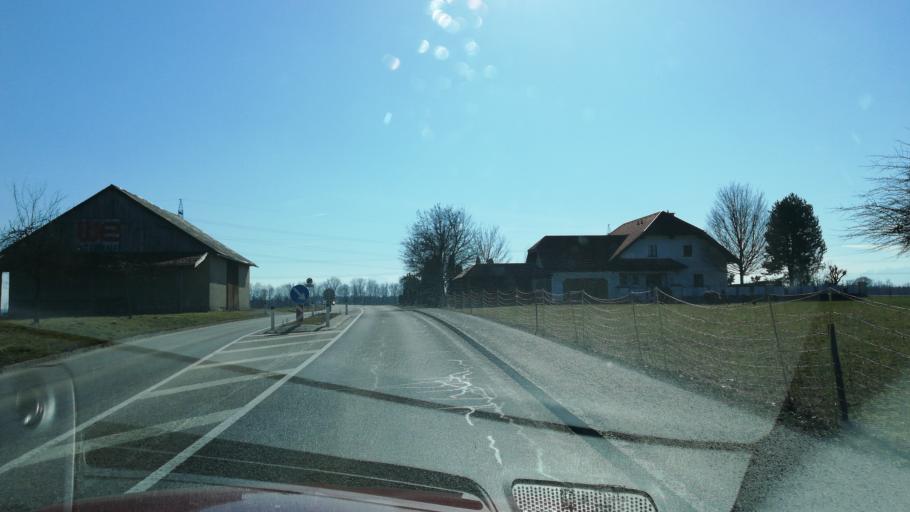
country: AT
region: Upper Austria
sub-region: Wels-Land
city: Neukirchen bei Lambach
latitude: 48.0926
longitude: 13.8387
